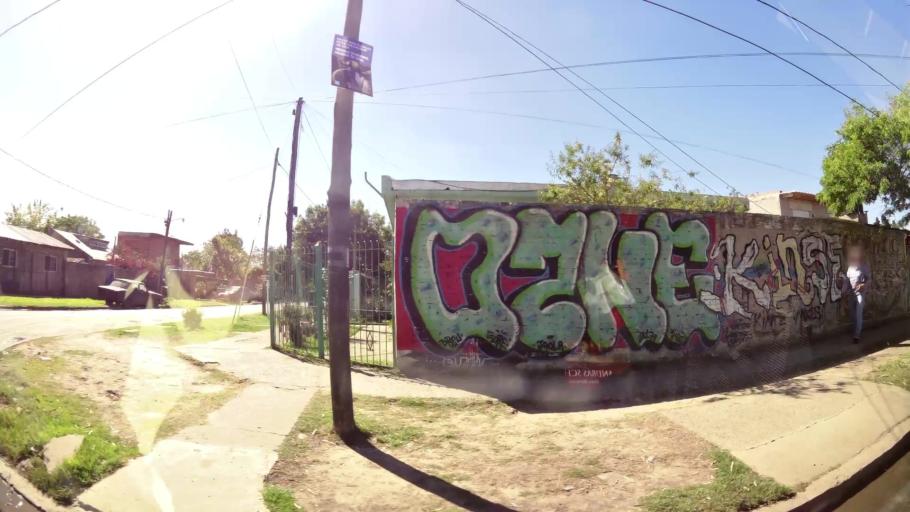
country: AR
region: Buenos Aires
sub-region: Partido de Almirante Brown
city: Adrogue
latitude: -34.7849
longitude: -58.3548
